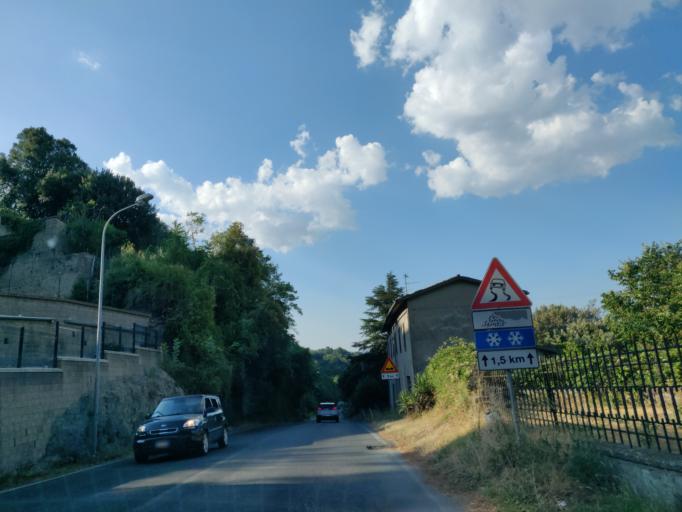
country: IT
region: Latium
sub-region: Provincia di Viterbo
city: Acquapendente
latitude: 42.7475
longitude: 11.8631
